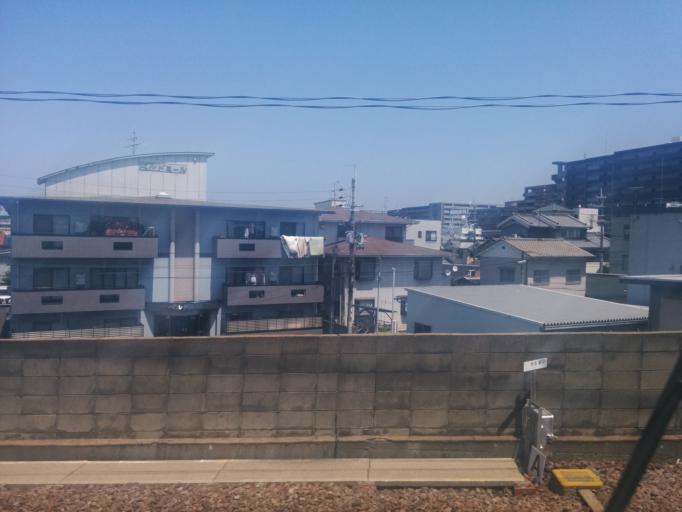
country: JP
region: Nara
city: Kashihara-shi
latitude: 34.5137
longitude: 135.7902
